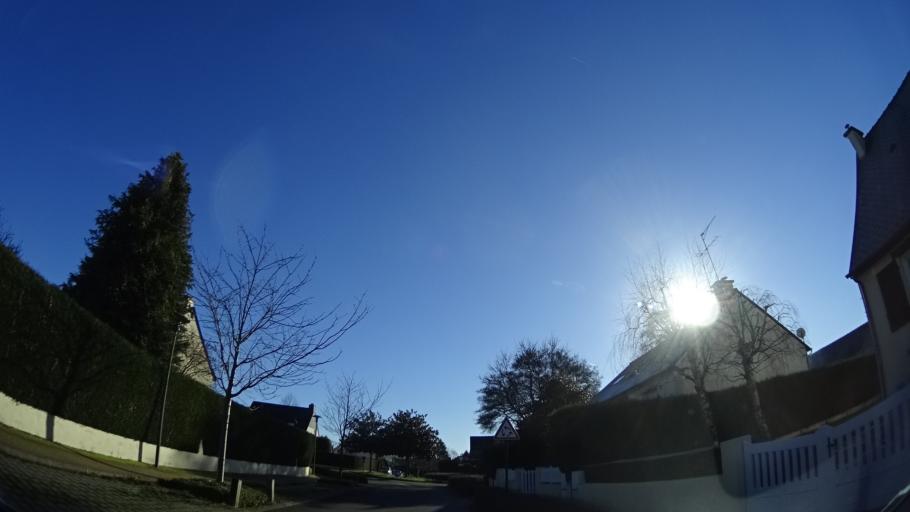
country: FR
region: Brittany
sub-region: Departement d'Ille-et-Vilaine
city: Chevaigne
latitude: 48.2115
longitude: -1.6292
